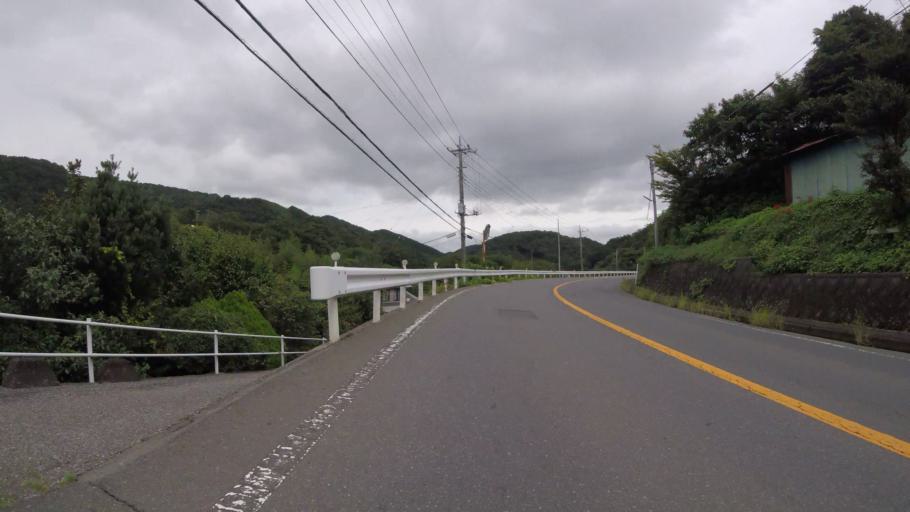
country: JP
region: Shizuoka
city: Ito
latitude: 35.0066
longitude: 138.9788
